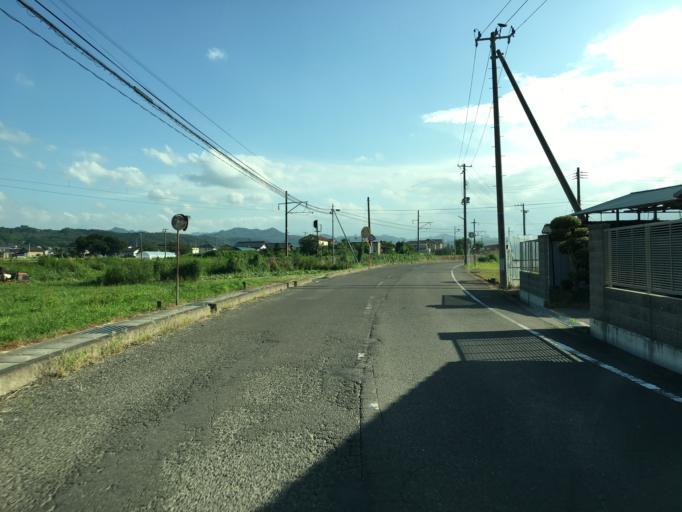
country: JP
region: Fukushima
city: Yanagawamachi-saiwaicho
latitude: 37.8302
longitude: 140.5829
